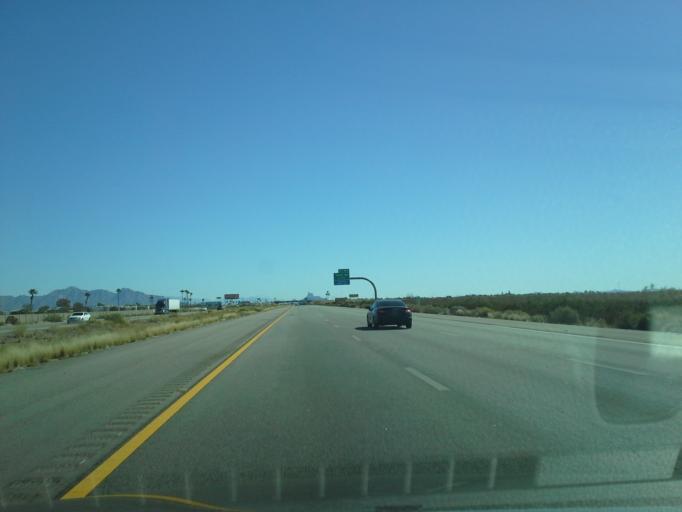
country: US
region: Arizona
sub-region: Pinal County
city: Arizona City
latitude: 32.7849
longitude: -111.6320
